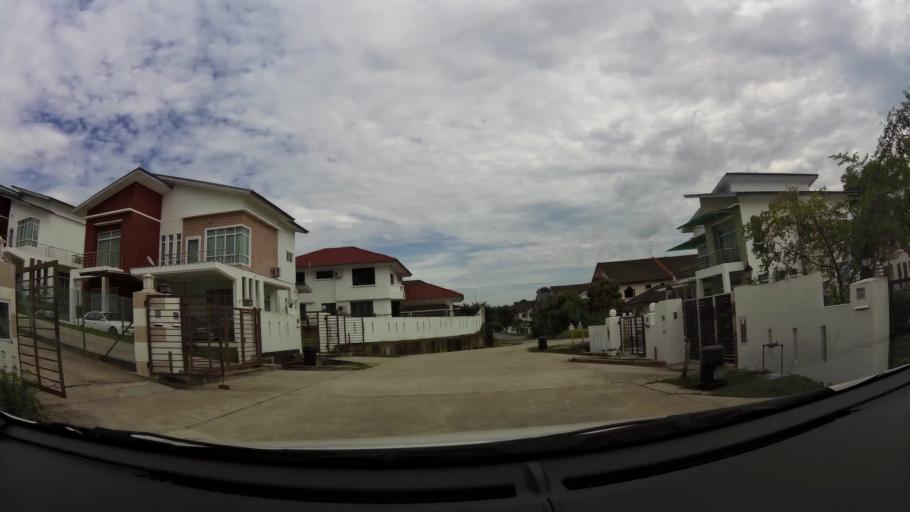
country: BN
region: Brunei and Muara
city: Bandar Seri Begawan
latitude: 4.8861
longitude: 114.8989
